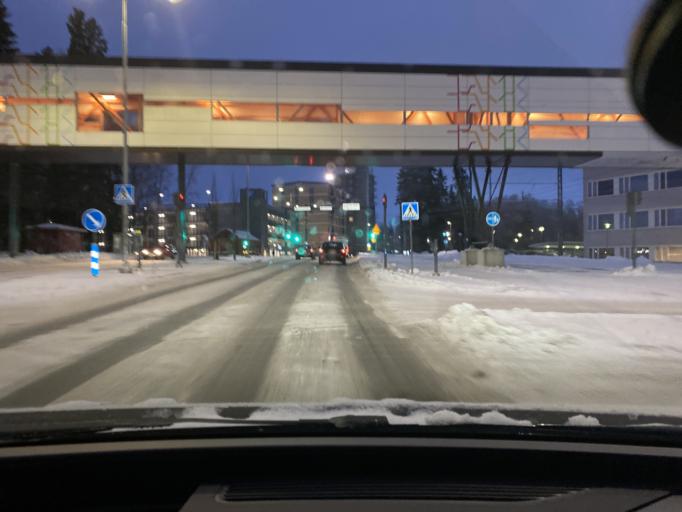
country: FI
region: Pirkanmaa
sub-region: Tampere
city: Tampere
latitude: 61.5044
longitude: 23.8102
